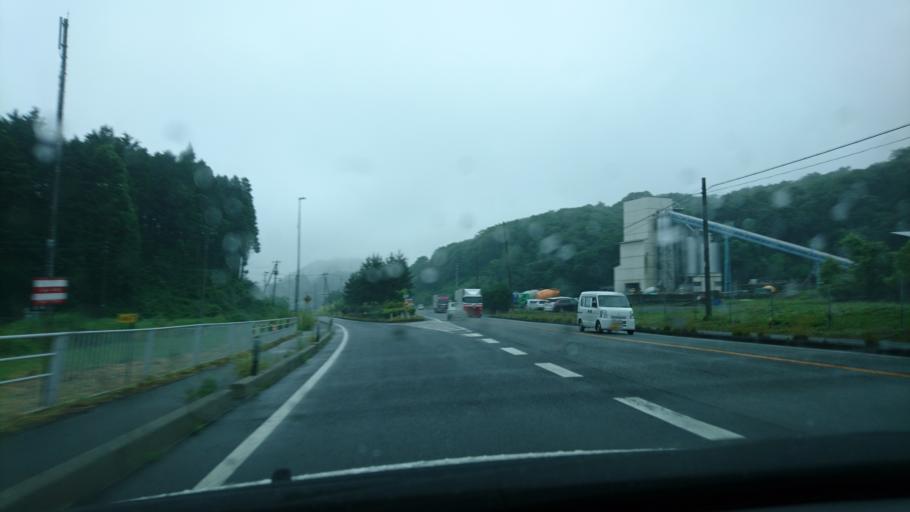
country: JP
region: Iwate
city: Ichinoseki
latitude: 38.8854
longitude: 141.1182
